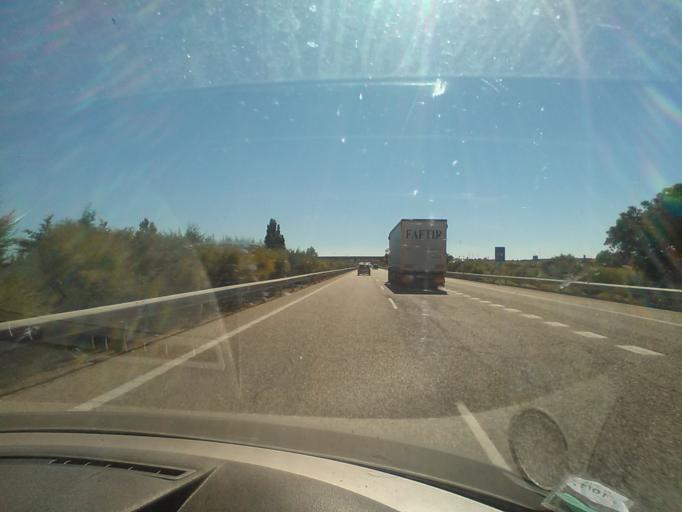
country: ES
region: Castille and Leon
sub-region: Provincia de Zamora
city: Quintanilla de Urz
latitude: 42.0221
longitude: -5.8479
